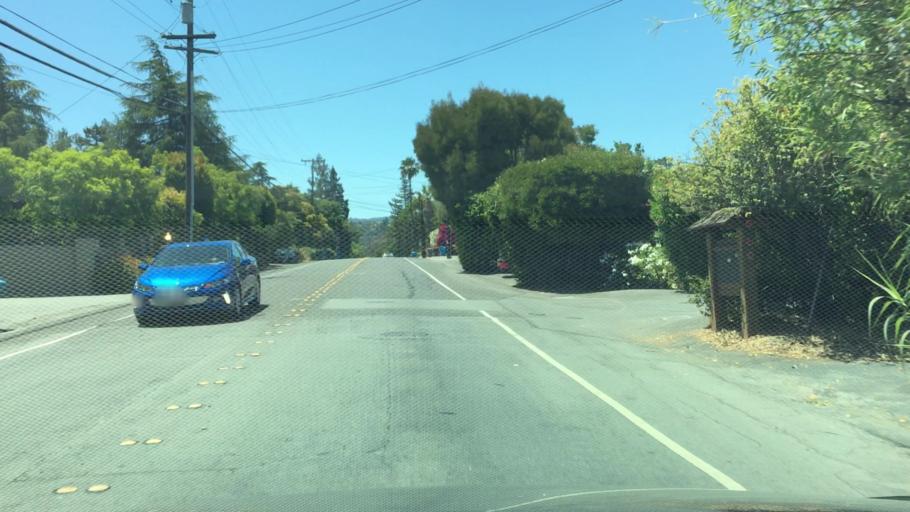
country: US
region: California
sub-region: San Mateo County
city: Emerald Lake Hills
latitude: 37.4821
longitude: -122.2568
